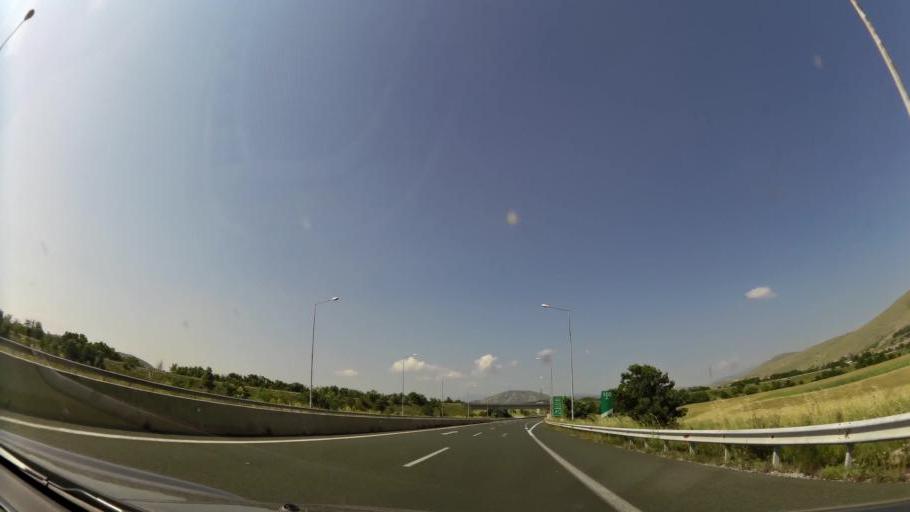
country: GR
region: West Macedonia
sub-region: Nomos Kozanis
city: Koila
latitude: 40.3510
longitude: 21.8088
